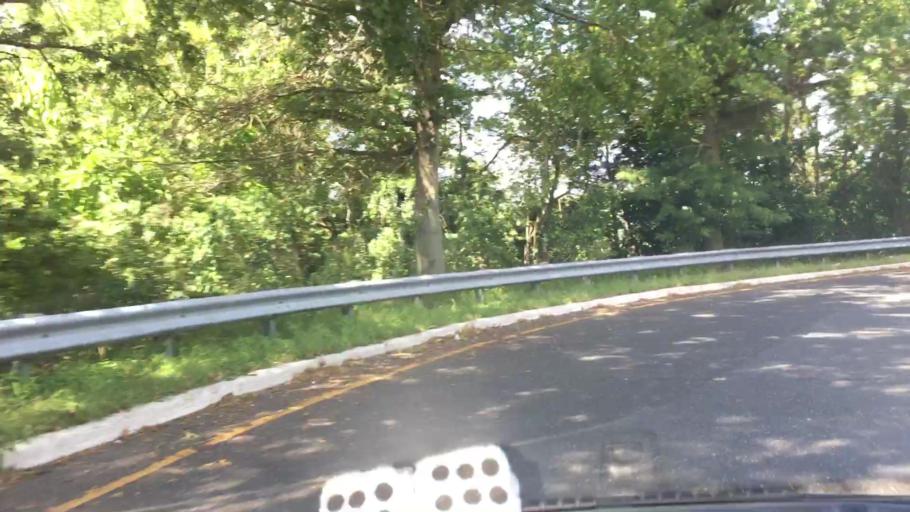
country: US
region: New Jersey
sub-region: Gloucester County
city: Turnersville
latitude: 39.7574
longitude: -75.0478
